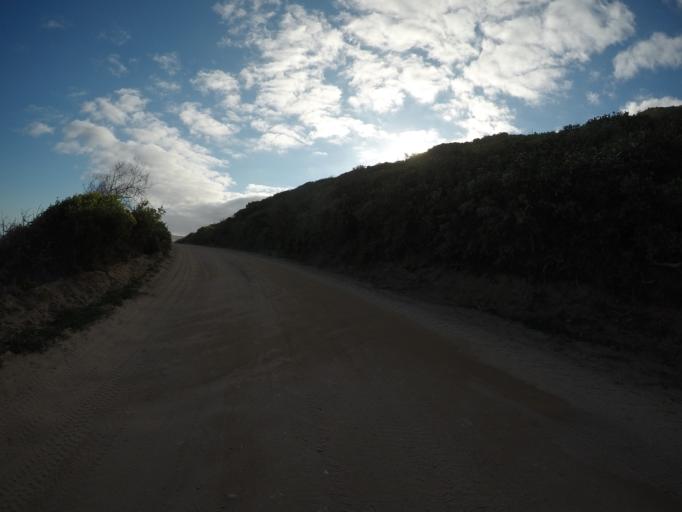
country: ZA
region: Western Cape
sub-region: Eden District Municipality
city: Riversdale
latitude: -34.4188
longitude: 21.3598
